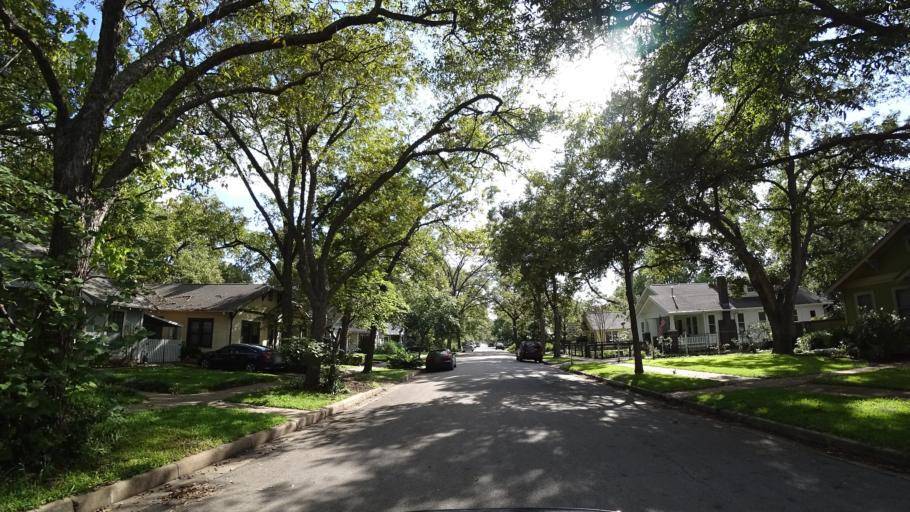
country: US
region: Texas
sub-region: Travis County
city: Austin
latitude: 30.3072
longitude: -97.7317
